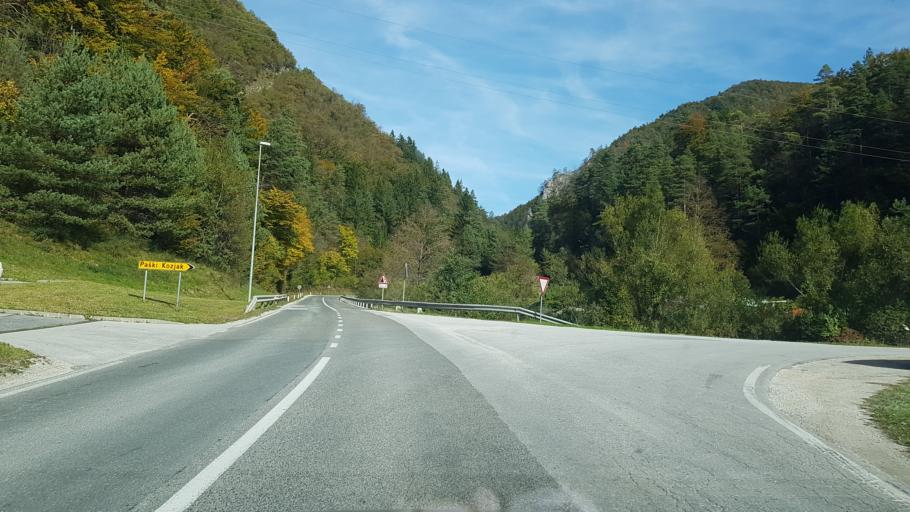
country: SI
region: Velenje
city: Velenje
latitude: 46.3854
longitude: 15.1607
